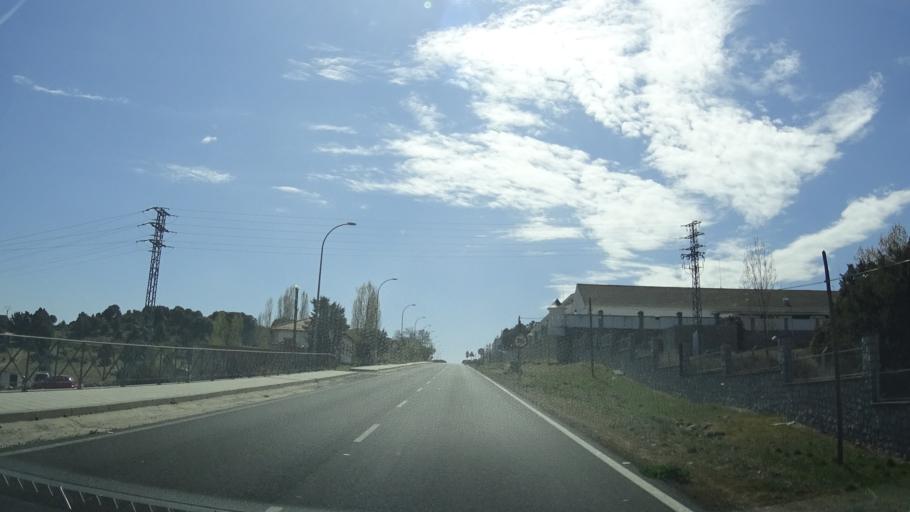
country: ES
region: Madrid
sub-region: Provincia de Madrid
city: Hoyo de Manzanares
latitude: 40.6268
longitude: -3.8795
